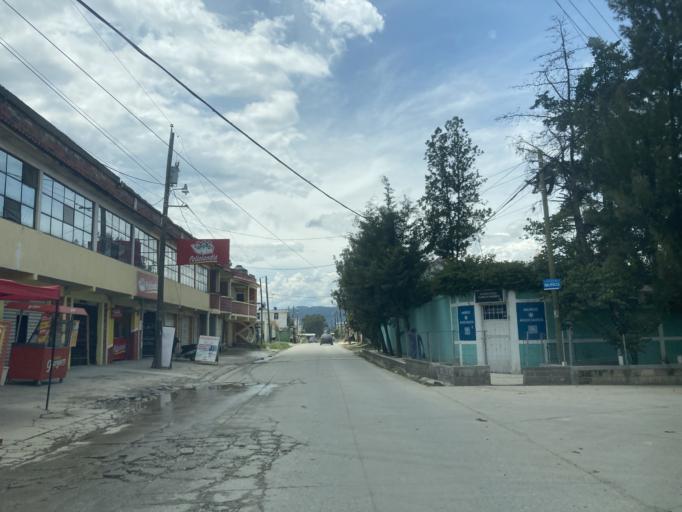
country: GT
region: Huehuetenango
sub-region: Municipio de Huehuetenango
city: Huehuetenango
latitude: 15.3262
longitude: -91.4932
